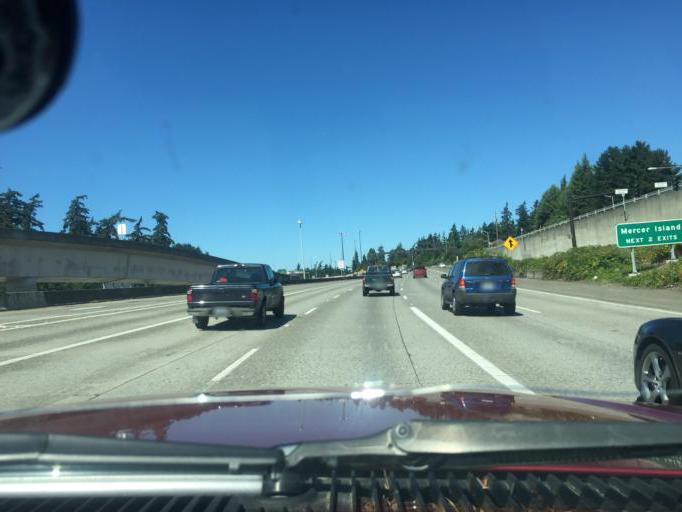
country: US
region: Washington
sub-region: King County
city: Newport
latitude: 47.5795
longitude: -122.1905
